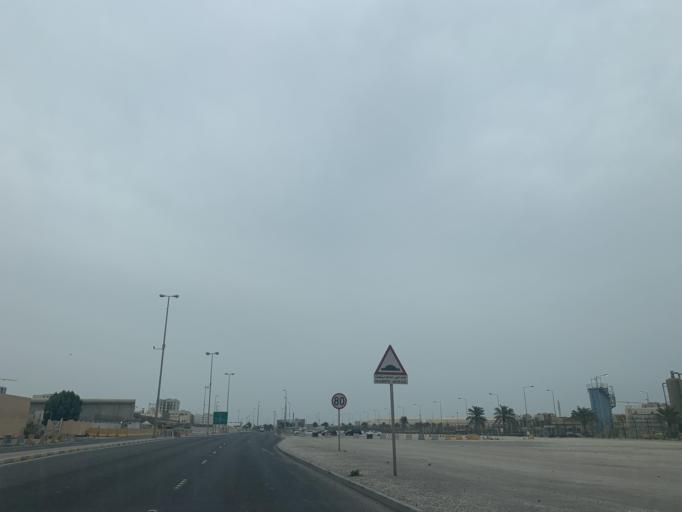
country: BH
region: Muharraq
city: Al Hadd
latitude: 26.2203
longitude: 50.6576
